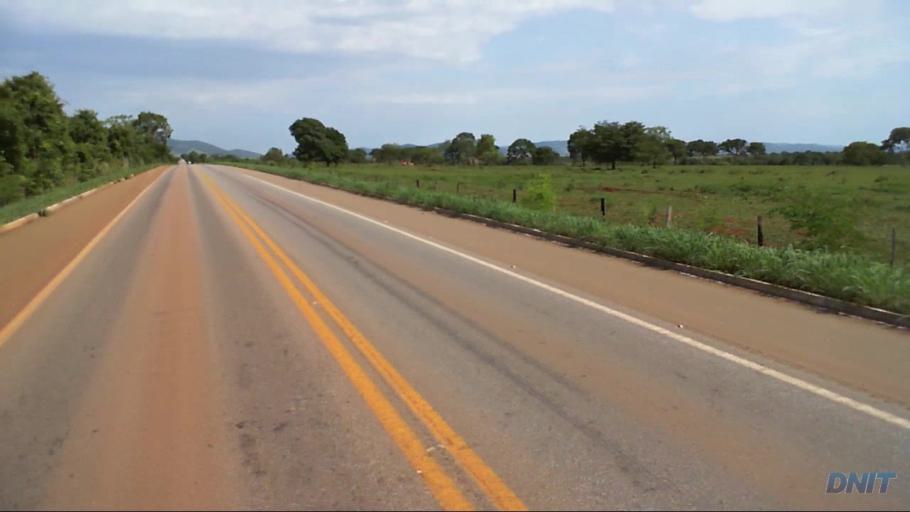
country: BR
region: Goias
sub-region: Barro Alto
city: Barro Alto
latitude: -15.0855
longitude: -48.8592
